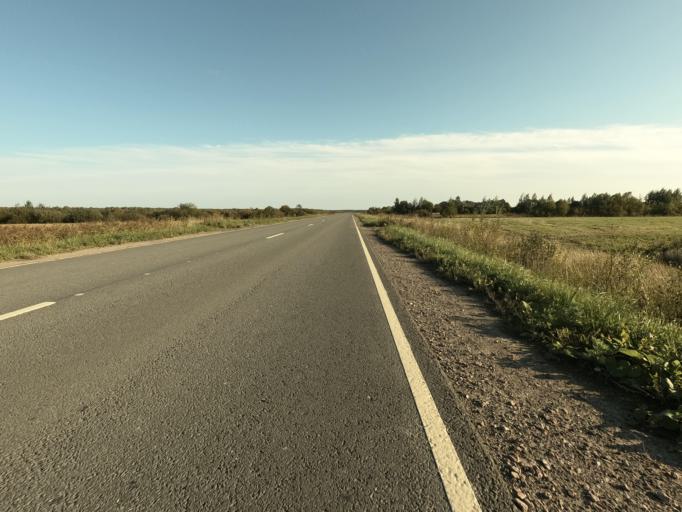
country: RU
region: St.-Petersburg
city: Sapernyy
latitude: 59.7476
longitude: 30.6421
